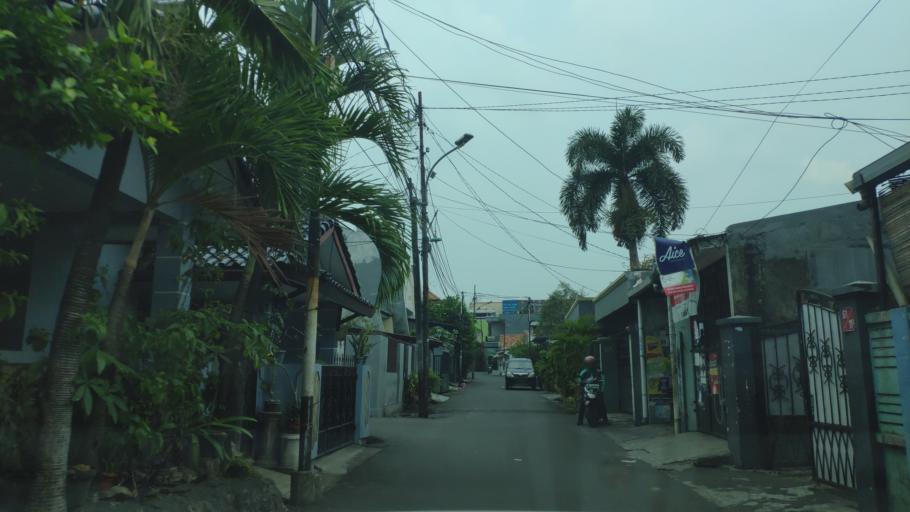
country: ID
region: Jakarta Raya
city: Jakarta
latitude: -6.1928
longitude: 106.8004
